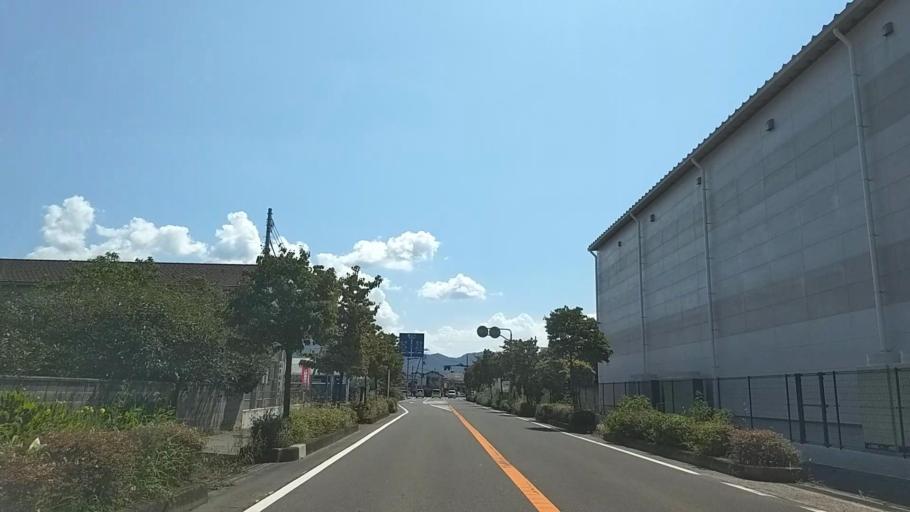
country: JP
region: Yamanashi
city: Ryuo
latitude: 35.5957
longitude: 138.5036
